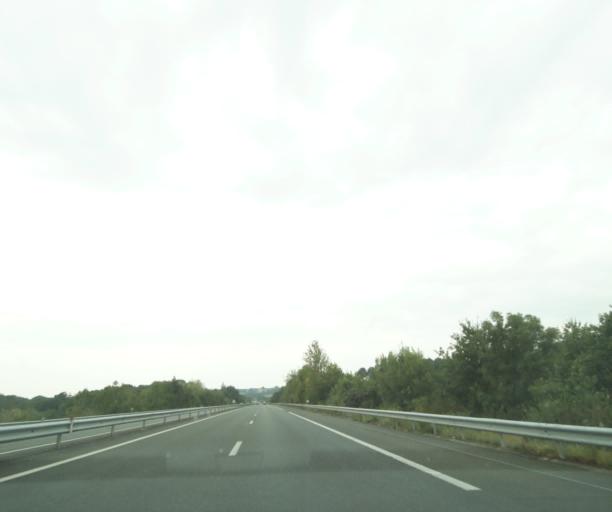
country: FR
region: Pays de la Loire
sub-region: Departement de la Vendee
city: Bournezeau
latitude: 46.6732
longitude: -1.1563
